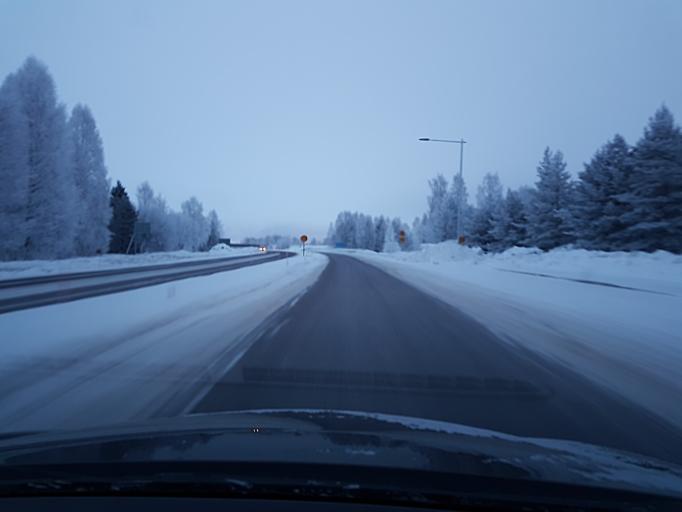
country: SE
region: Norrbotten
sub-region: Pitea Kommun
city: Bergsviken
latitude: 65.3130
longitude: 21.4008
